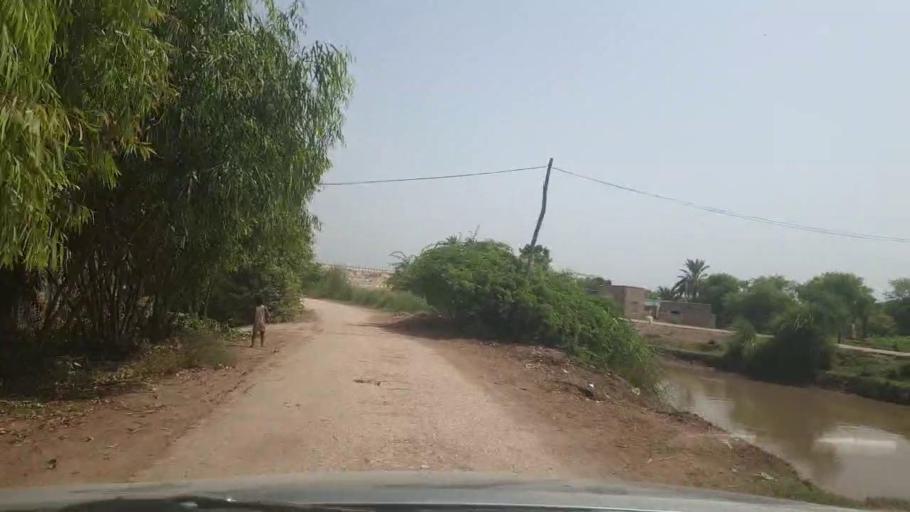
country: PK
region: Sindh
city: Pano Aqil
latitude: 27.9020
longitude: 69.1473
